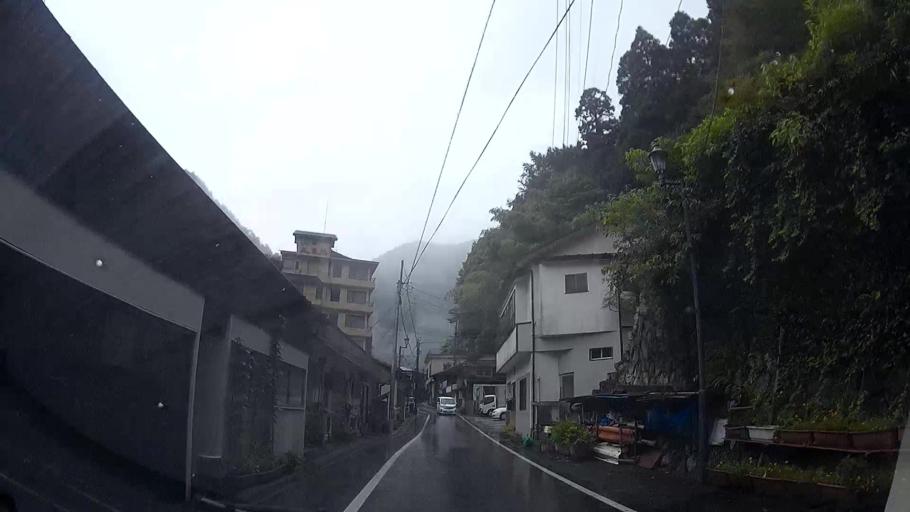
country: JP
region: Oita
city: Tsukawaki
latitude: 33.1840
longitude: 131.0334
